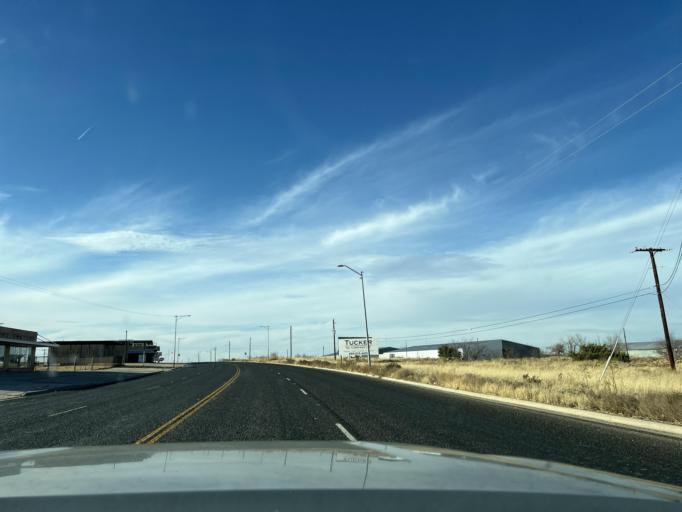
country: US
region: Texas
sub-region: Scurry County
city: Snyder
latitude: 32.7109
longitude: -100.8904
